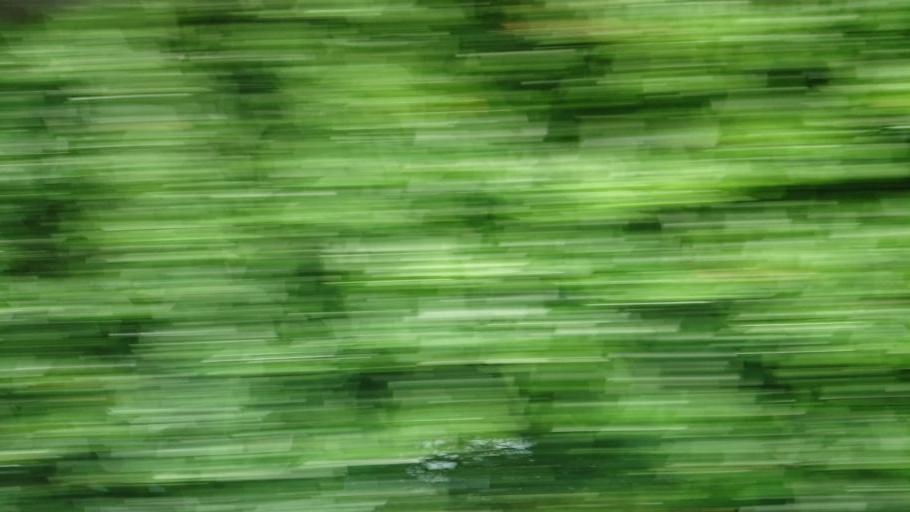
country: GB
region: England
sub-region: North Yorkshire
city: Ingleton
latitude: 54.1462
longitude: -2.4911
